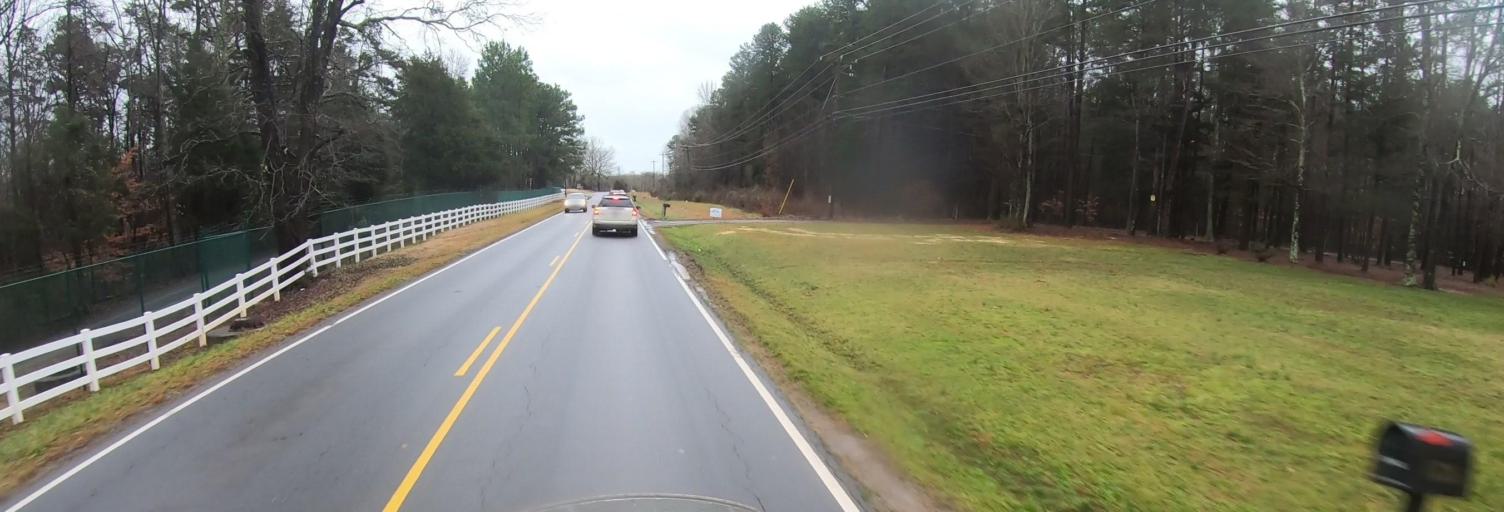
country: US
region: South Carolina
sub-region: York County
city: Lake Wylie
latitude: 35.0855
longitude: -81.0047
